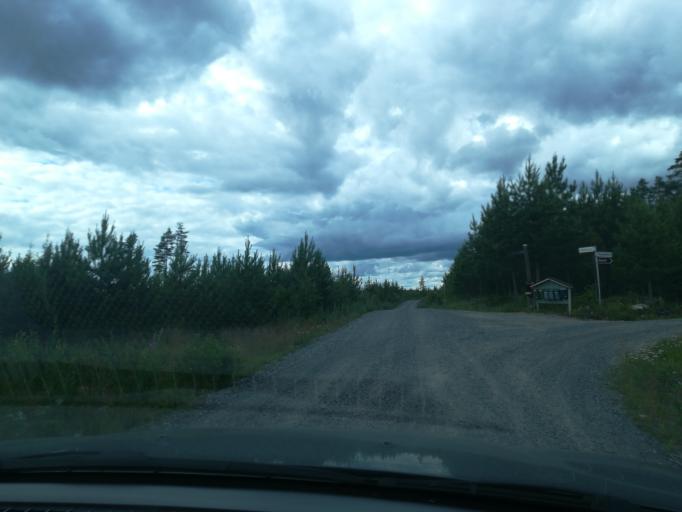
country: FI
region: Southern Savonia
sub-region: Mikkeli
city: Mikkeli
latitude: 61.6694
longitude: 27.1196
